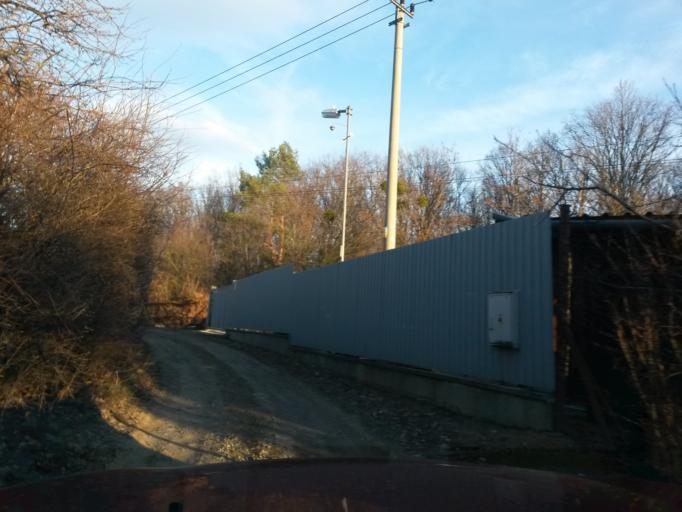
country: SK
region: Kosicky
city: Kosice
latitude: 48.7058
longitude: 21.2943
